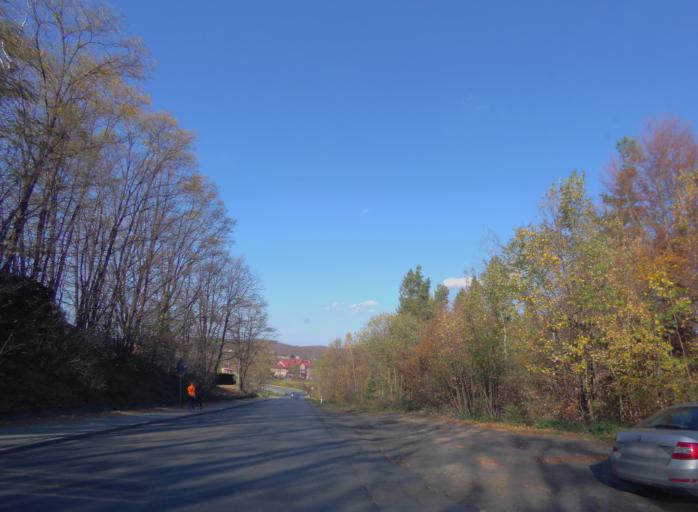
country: PL
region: Subcarpathian Voivodeship
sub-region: Powiat leski
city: Polanczyk
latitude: 49.3738
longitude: 22.4180
